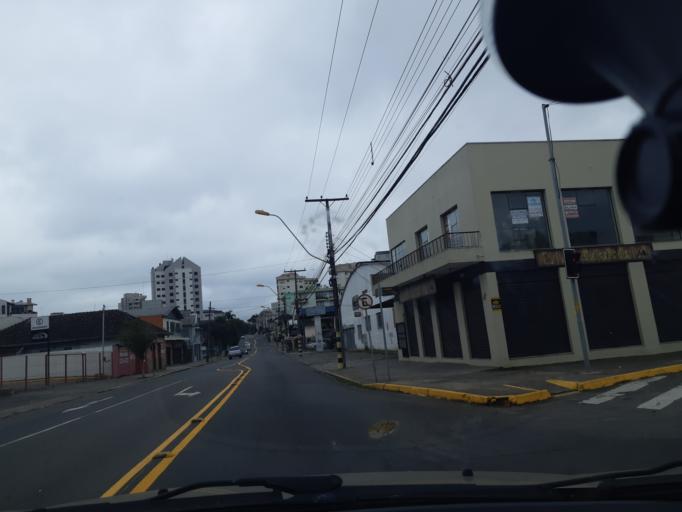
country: BR
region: Rio Grande do Sul
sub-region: Caxias Do Sul
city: Caxias do Sul
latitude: -29.1602
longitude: -51.1939
